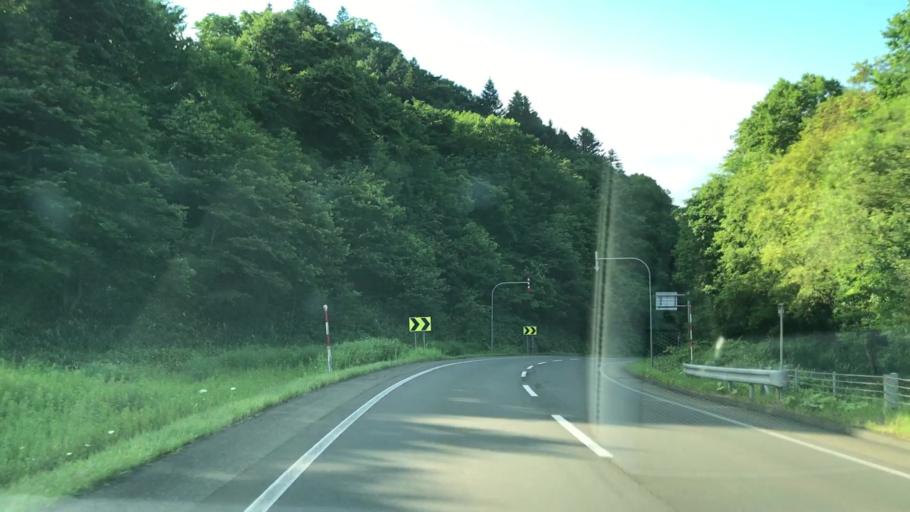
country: JP
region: Hokkaido
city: Chitose
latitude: 42.8859
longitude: 142.1227
